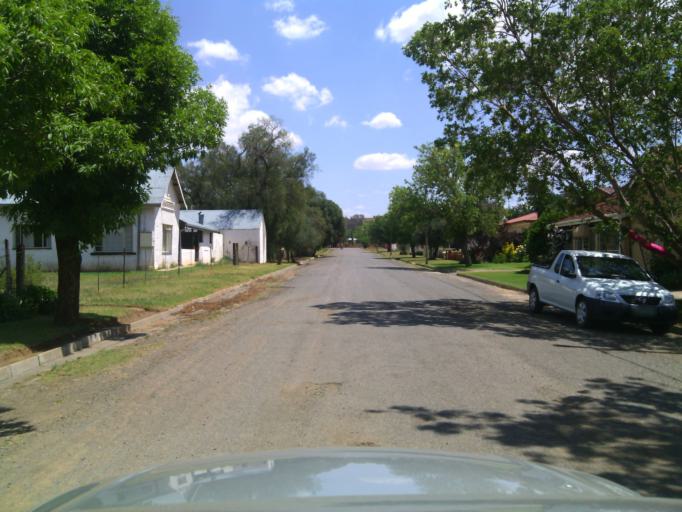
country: ZA
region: Orange Free State
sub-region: Xhariep District Municipality
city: Dewetsdorp
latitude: -29.5810
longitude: 26.6665
